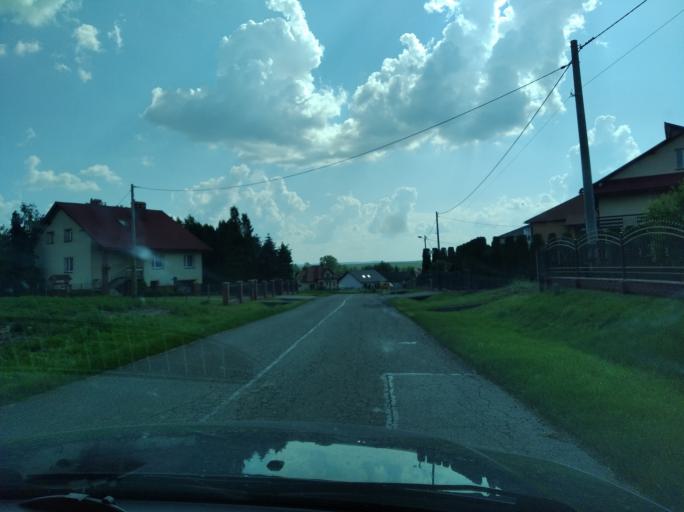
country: PL
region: Subcarpathian Voivodeship
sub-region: Powiat jaroslawski
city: Ostrow
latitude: 49.9423
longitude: 22.7534
